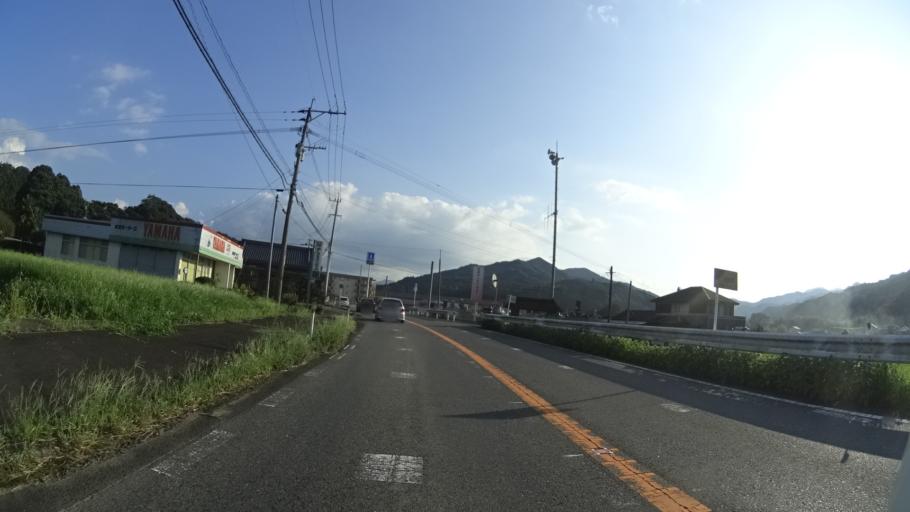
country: JP
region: Oita
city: Bungo-Takada-shi
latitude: 33.4563
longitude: 131.3288
